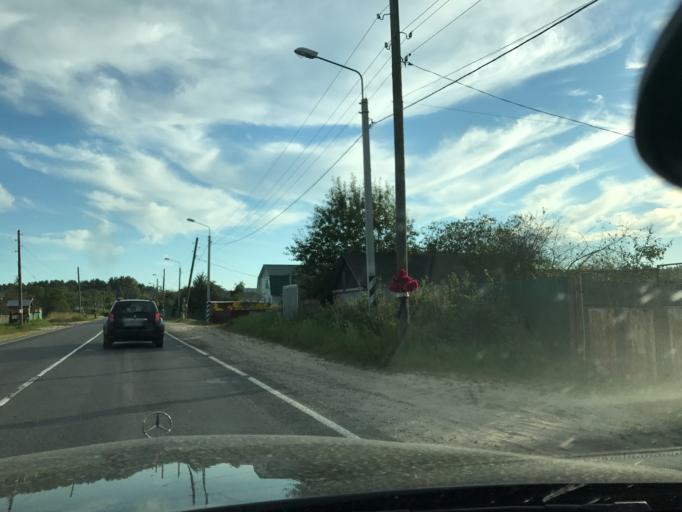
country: RU
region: Vladimir
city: Raduzhnyy
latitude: 56.0160
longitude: 40.3137
